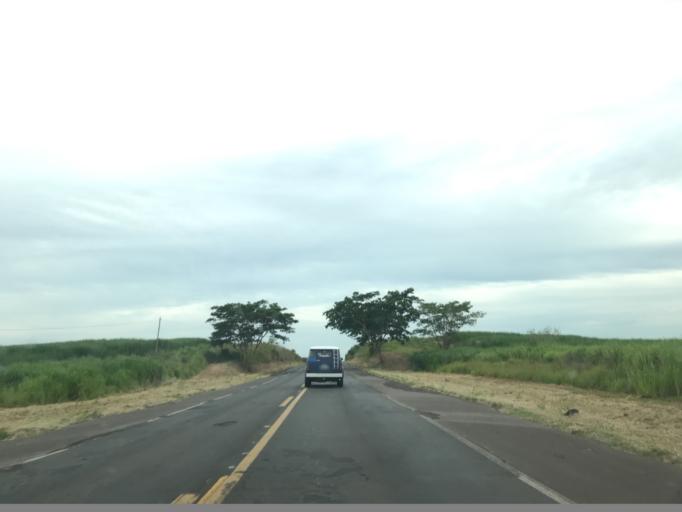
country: BR
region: Sao Paulo
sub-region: Tupa
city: Tupa
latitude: -21.6307
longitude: -50.4900
